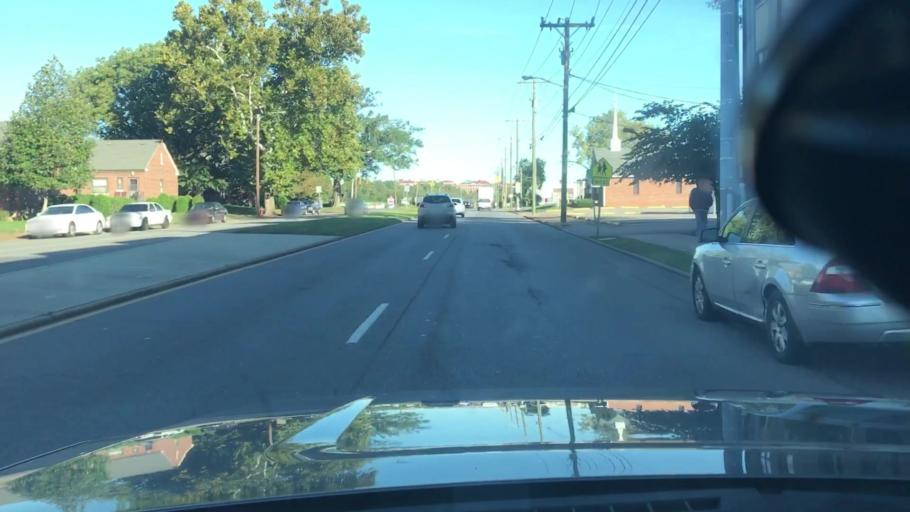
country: US
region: Tennessee
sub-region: Davidson County
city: Nashville
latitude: 36.1792
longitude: -86.7953
